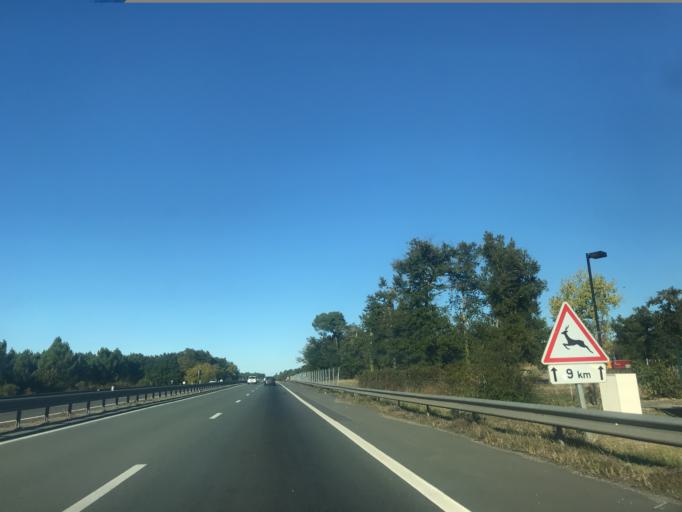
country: FR
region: Aquitaine
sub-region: Departement de la Gironde
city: Laruscade
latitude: 45.1696
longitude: -0.3359
